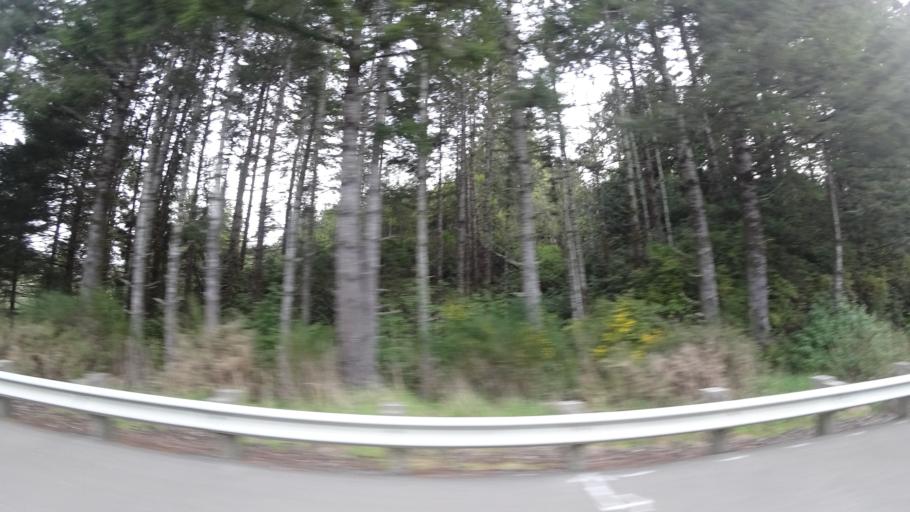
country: US
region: Oregon
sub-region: Coos County
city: Bandon
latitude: 43.1927
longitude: -124.3451
